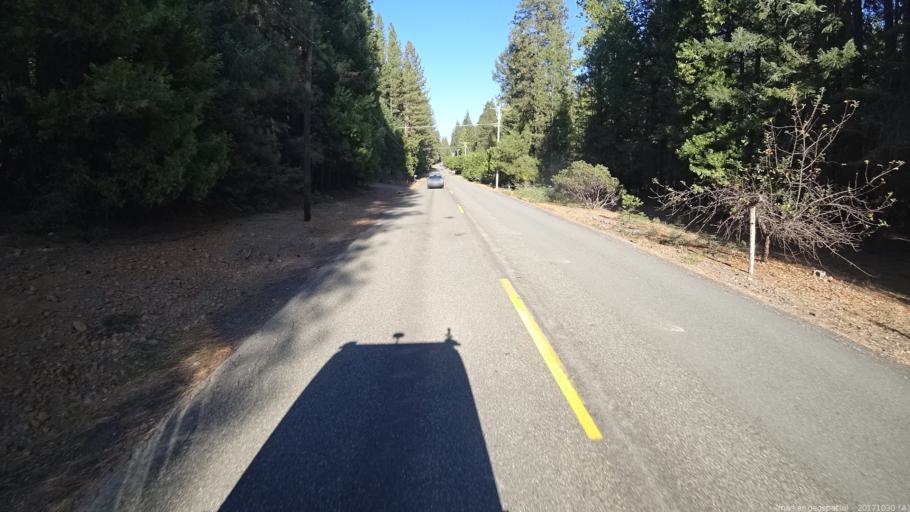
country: US
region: California
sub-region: Shasta County
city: Shingletown
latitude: 40.5306
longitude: -121.7449
